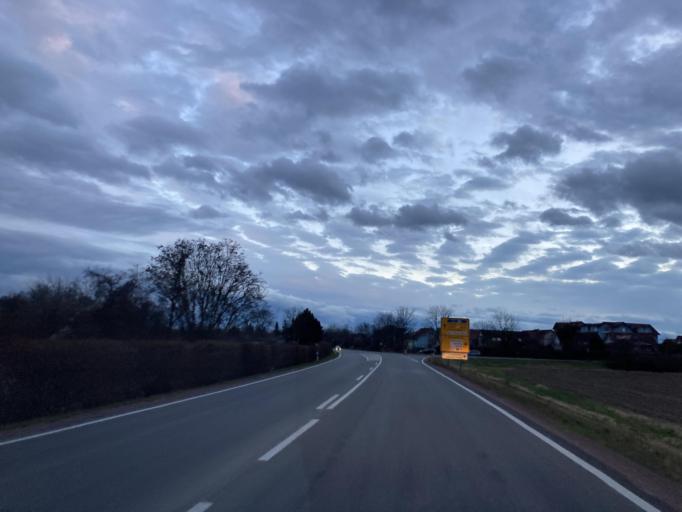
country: DE
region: Baden-Wuerttemberg
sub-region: Freiburg Region
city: Breisach am Rhein
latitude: 48.0452
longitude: 7.5875
